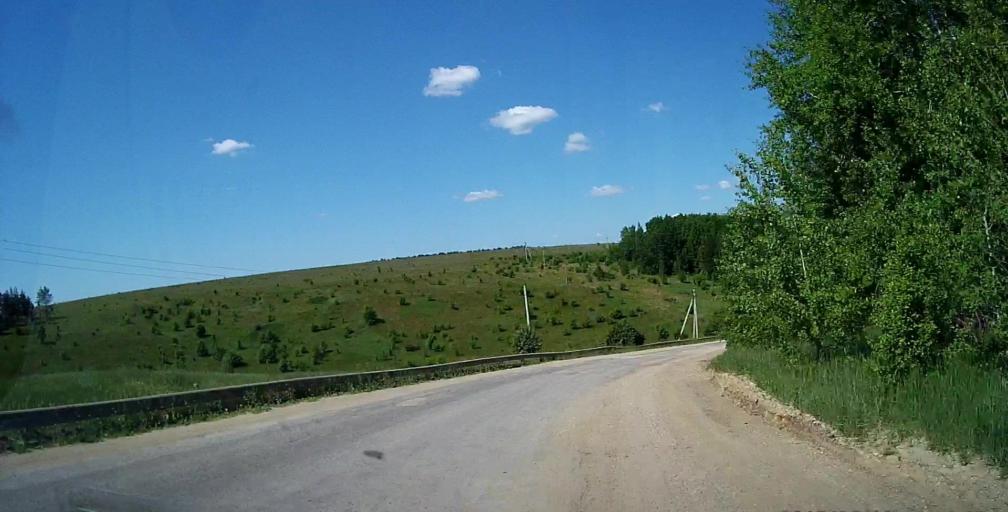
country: RU
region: Tula
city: Kurkino
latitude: 53.1981
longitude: 38.5753
